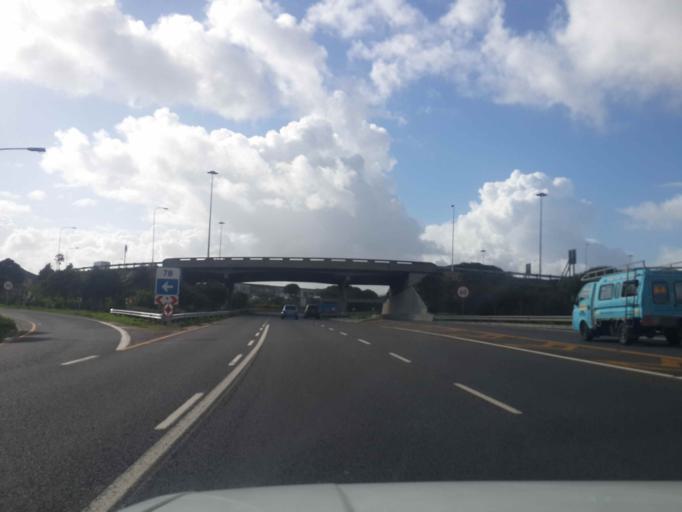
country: ZA
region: Western Cape
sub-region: City of Cape Town
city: Rosebank
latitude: -33.9174
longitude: 18.4793
